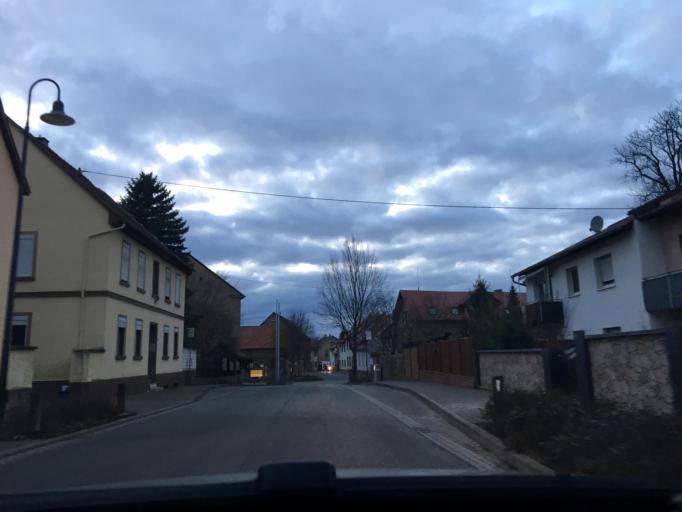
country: DE
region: Rheinland-Pfalz
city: Erbes-Budesheim
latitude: 49.7549
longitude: 8.0333
